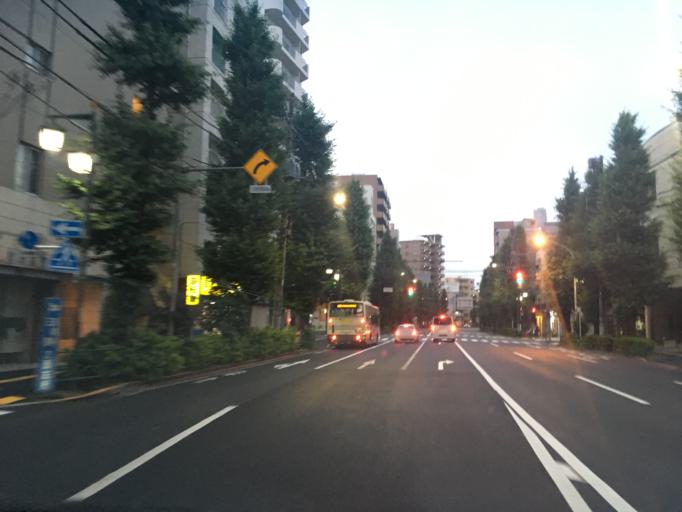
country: JP
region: Tokyo
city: Musashino
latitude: 35.7120
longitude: 139.6025
